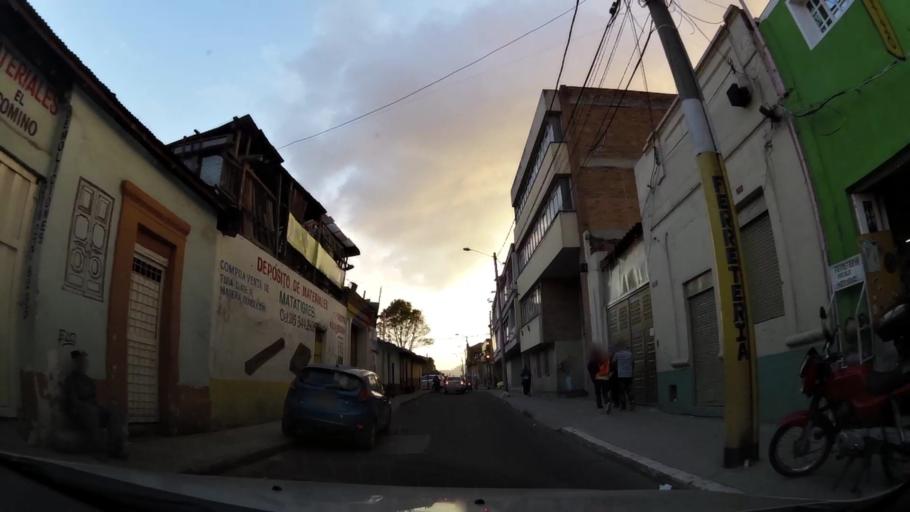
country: CO
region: Bogota D.C.
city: Bogota
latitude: 4.5902
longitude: -74.0813
